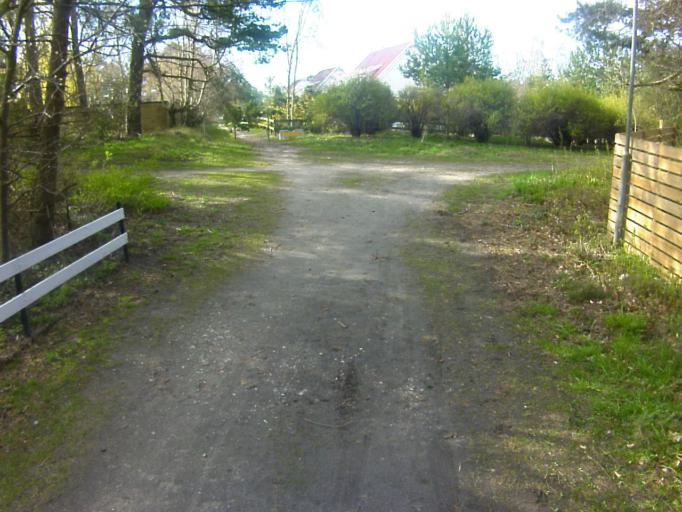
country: SE
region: Skane
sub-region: Kavlinge Kommun
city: Hofterup
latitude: 55.7976
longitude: 12.9800
